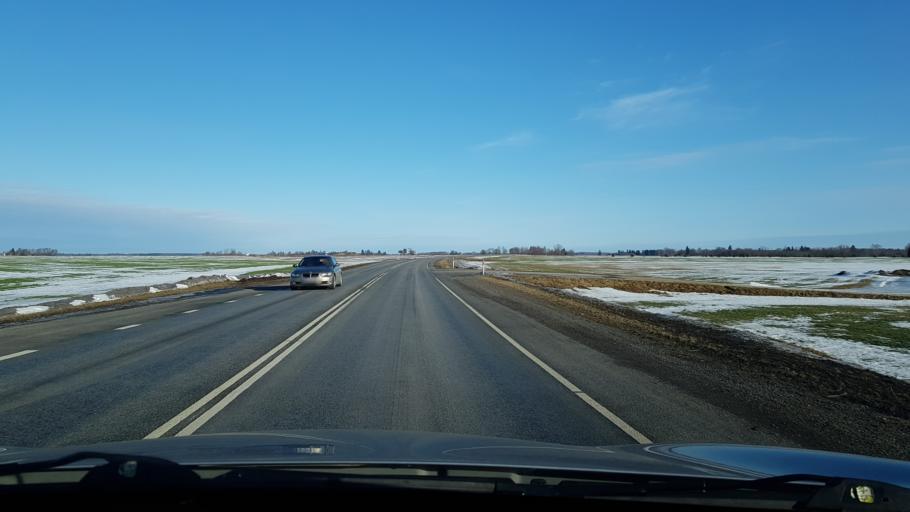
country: EE
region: Viljandimaa
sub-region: Vohma linn
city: Vohma
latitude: 58.6421
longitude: 25.5782
